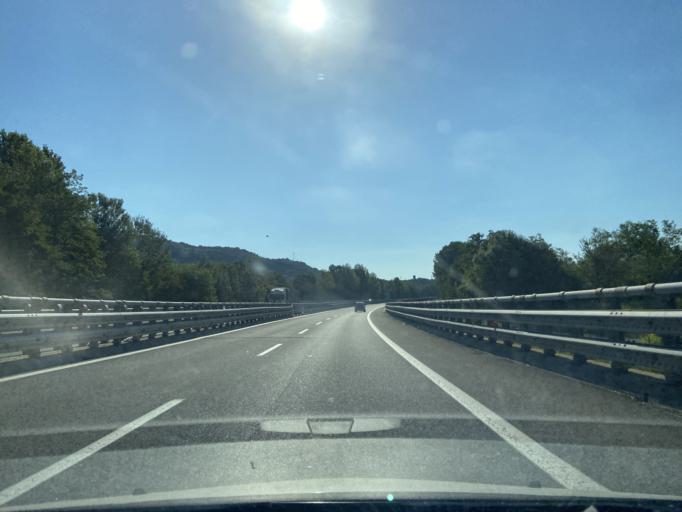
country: IT
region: Piedmont
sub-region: Provincia di Torino
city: Sant'Ambrogio di Torino
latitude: 45.1114
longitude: 7.3539
